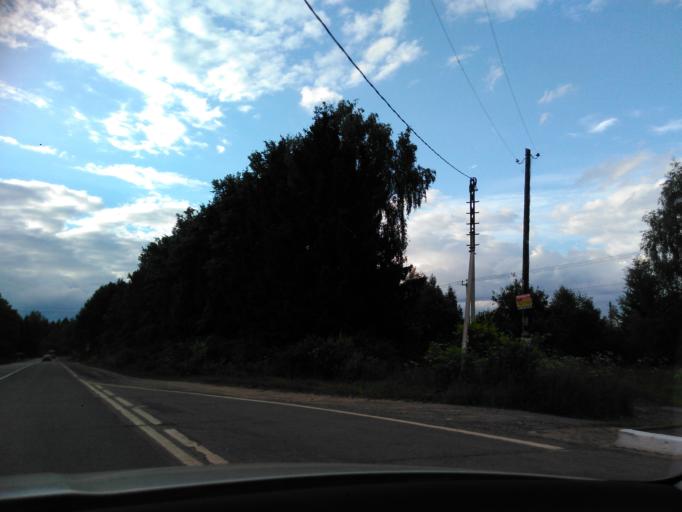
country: RU
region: Moskovskaya
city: Solnechnogorsk
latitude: 56.1366
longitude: 36.9196
